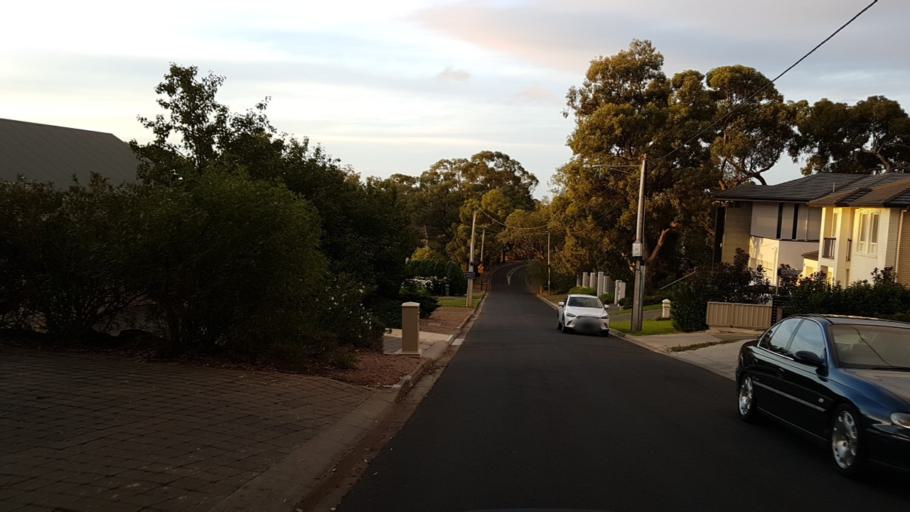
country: AU
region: South Australia
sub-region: Burnside
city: Beaumont
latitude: -34.9418
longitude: 138.6683
